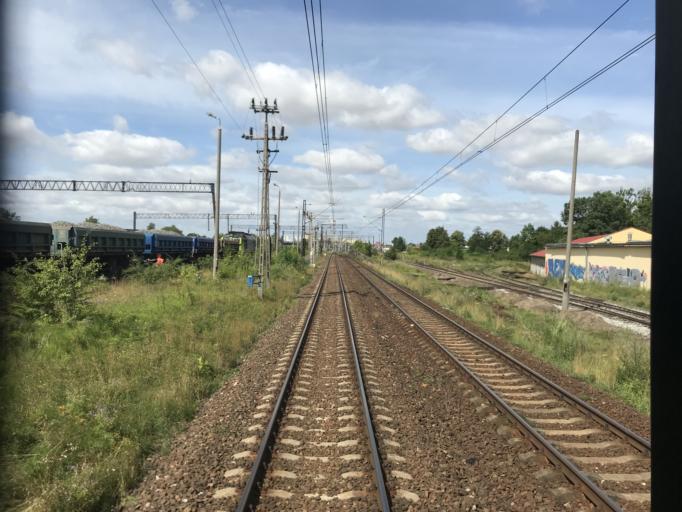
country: PL
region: Pomeranian Voivodeship
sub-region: Powiat malborski
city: Malbork
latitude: 54.0341
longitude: 19.0603
